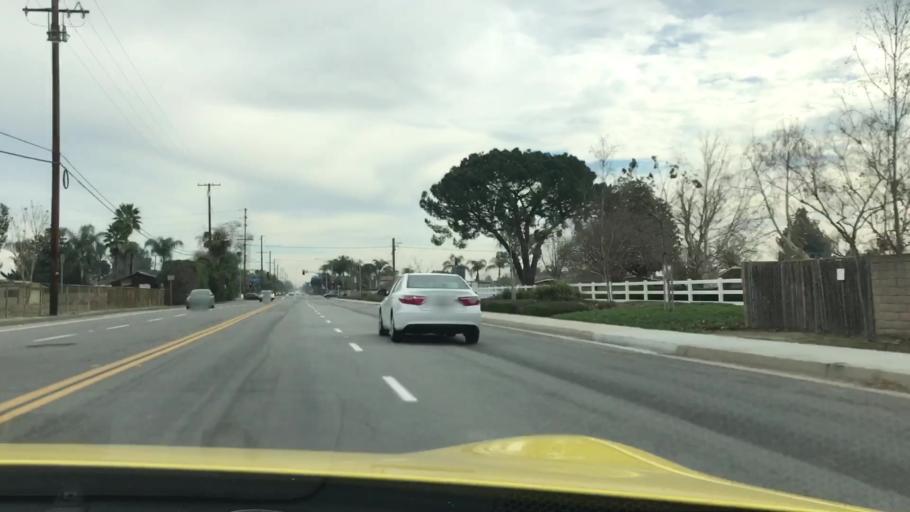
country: US
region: California
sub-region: San Bernardino County
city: Chino Hills
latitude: 34.0115
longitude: -117.7264
